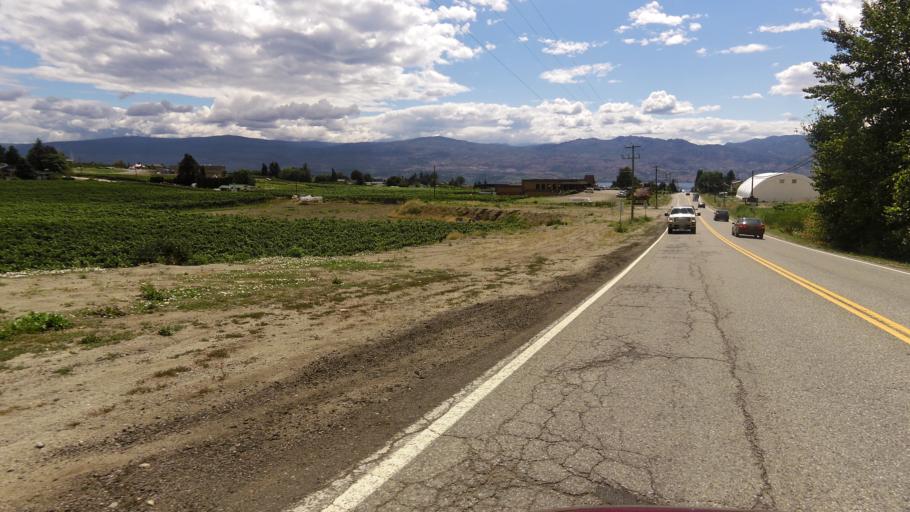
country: CA
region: British Columbia
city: West Kelowna
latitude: 49.8578
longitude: -119.5557
